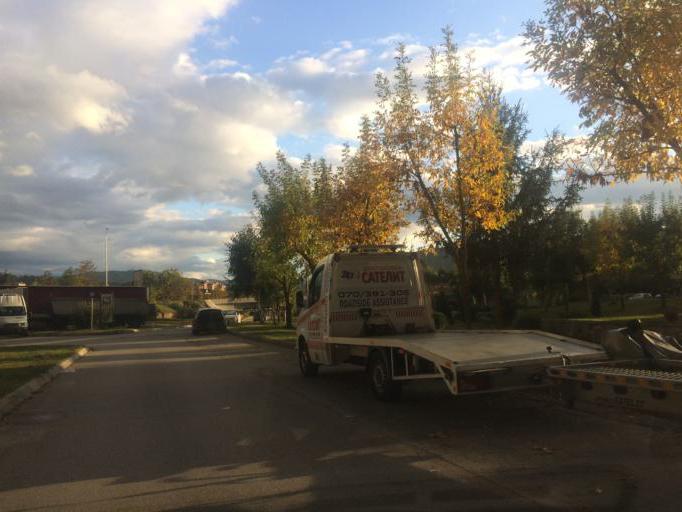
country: MK
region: Makedonska Kamenica
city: Makedonska Kamenica
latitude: 42.0248
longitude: 22.5875
